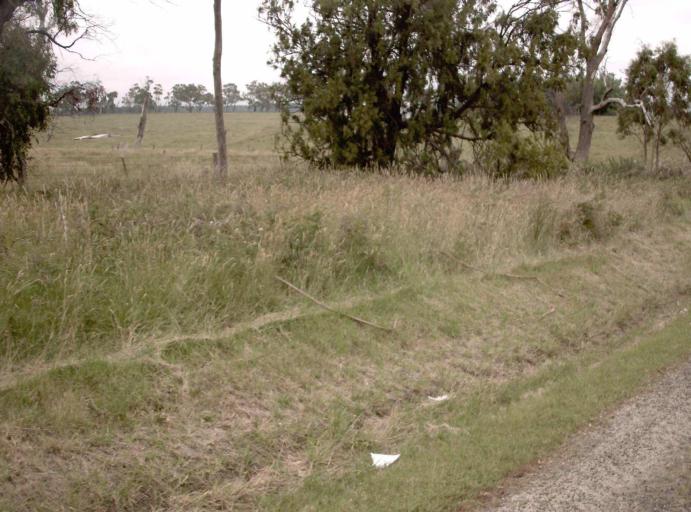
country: AU
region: Victoria
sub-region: Latrobe
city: Traralgon
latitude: -38.2408
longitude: 146.5054
